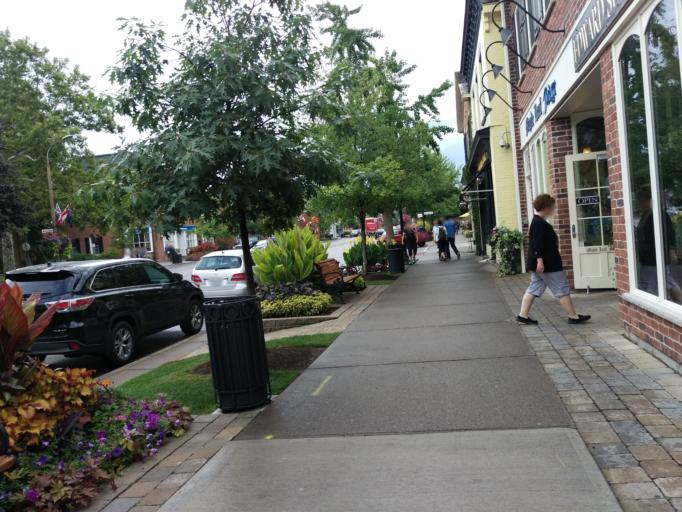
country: US
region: New York
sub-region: Niagara County
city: Youngstown
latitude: 43.2564
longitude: -79.0744
